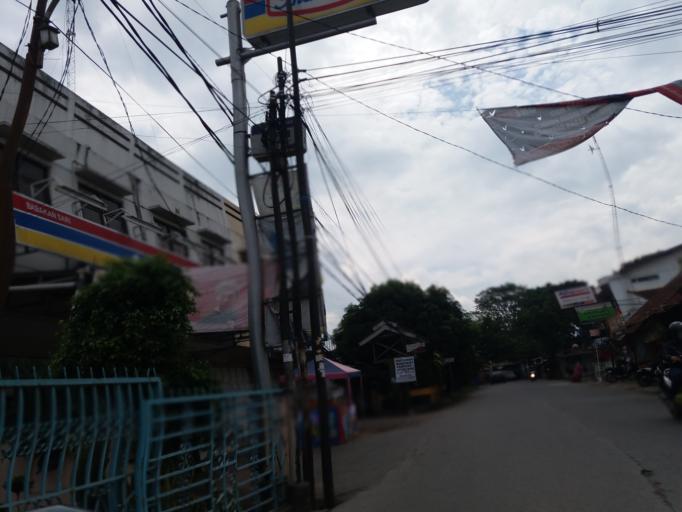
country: ID
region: West Java
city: Bandung
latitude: -6.9254
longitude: 107.6543
